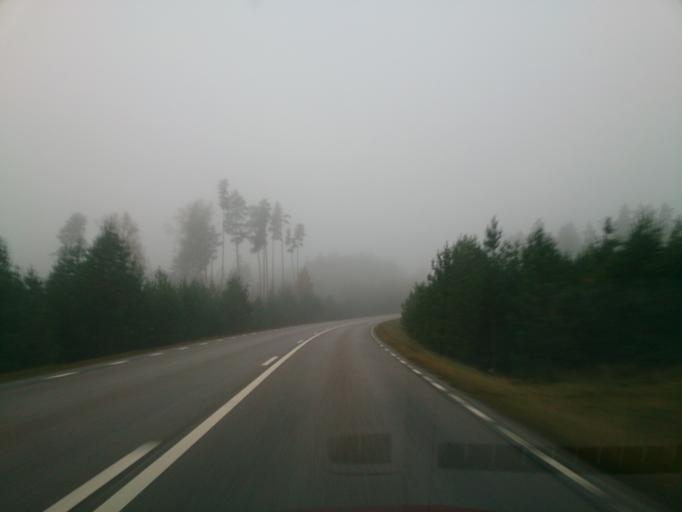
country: SE
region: OEstergoetland
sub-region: Atvidabergs Kommun
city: Atvidaberg
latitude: 58.1743
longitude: 15.9707
